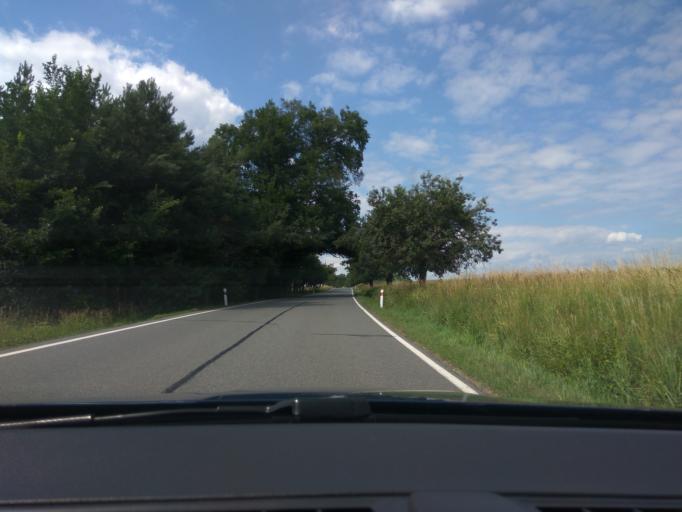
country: CZ
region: Jihocesky
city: Bernartice
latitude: 49.3996
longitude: 14.3632
